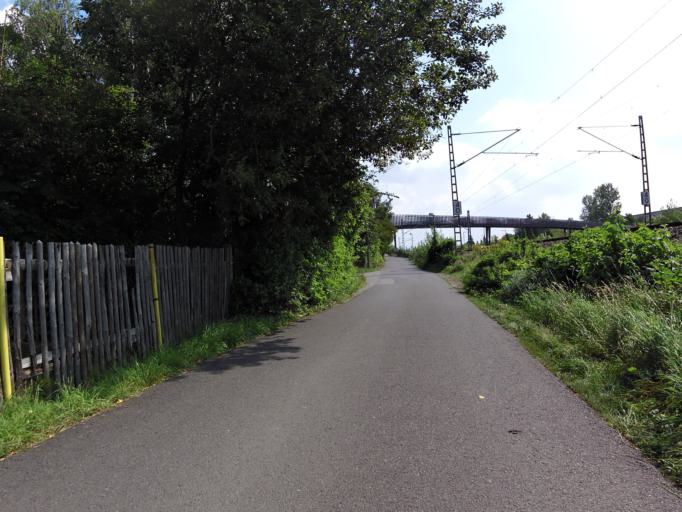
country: DE
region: Saxony
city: Leipzig
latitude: 51.3760
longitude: 12.3356
